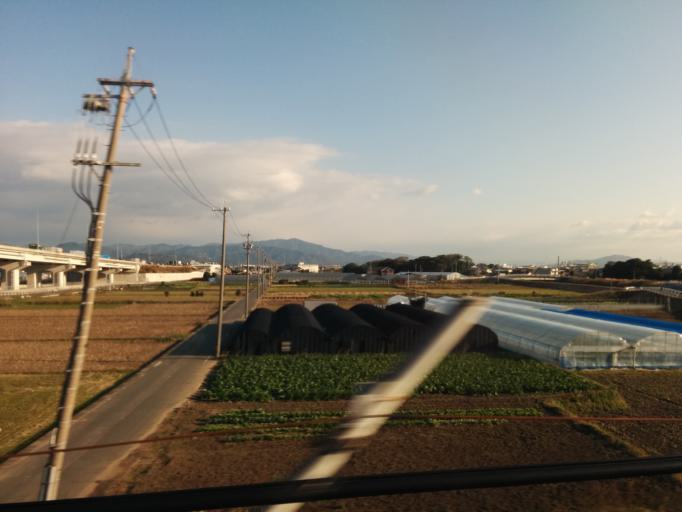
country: JP
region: Aichi
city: Kozakai-cho
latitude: 34.7966
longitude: 137.3323
